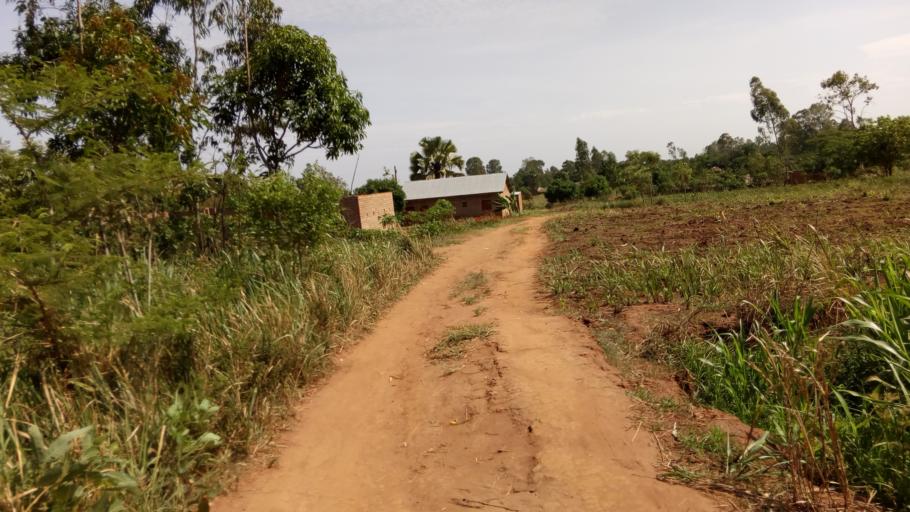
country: UG
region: Northern Region
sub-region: Gulu District
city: Gulu
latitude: 2.7954
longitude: 32.3191
